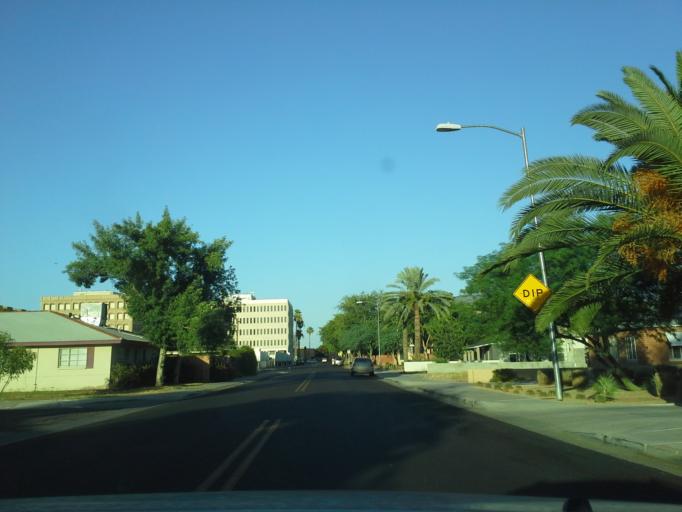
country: US
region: Arizona
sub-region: Maricopa County
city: Phoenix
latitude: 33.5021
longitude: -112.0770
